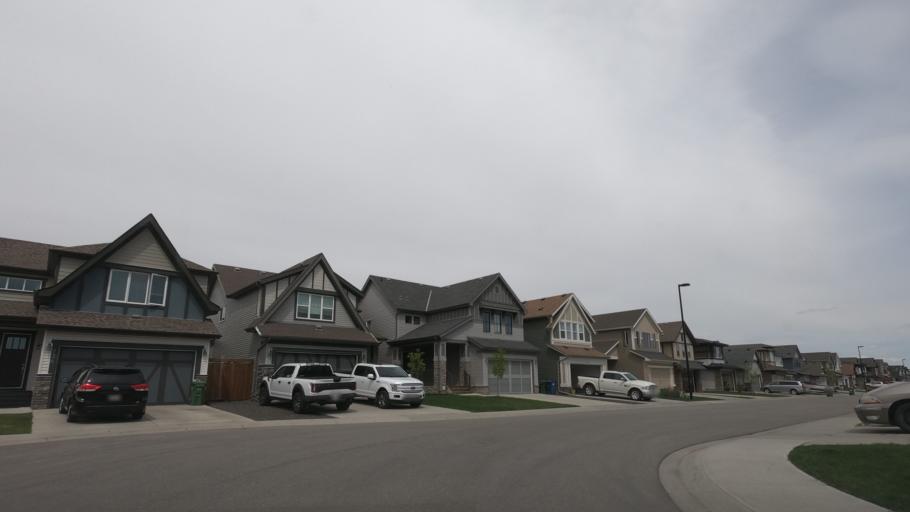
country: CA
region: Alberta
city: Airdrie
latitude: 51.3069
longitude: -114.0406
